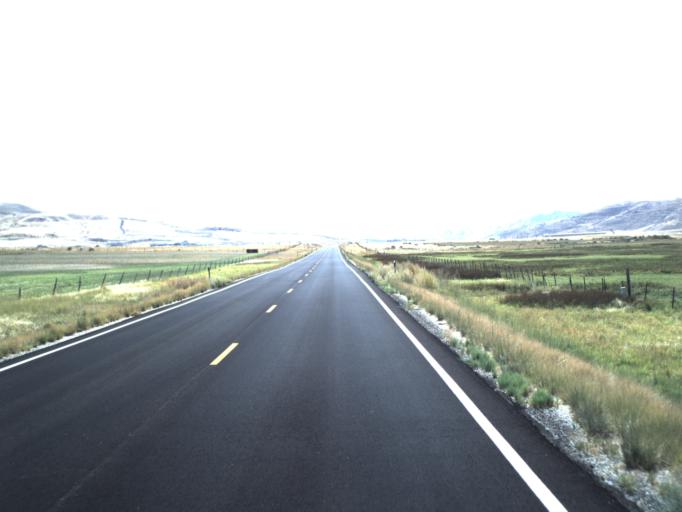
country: US
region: Utah
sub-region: Box Elder County
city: Tremonton
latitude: 41.7405
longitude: -112.4342
